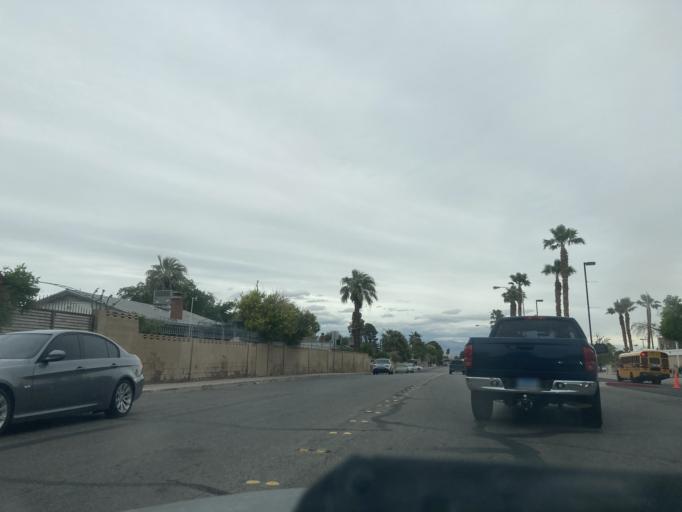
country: US
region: Nevada
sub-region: Clark County
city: Winchester
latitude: 36.1192
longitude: -115.0885
